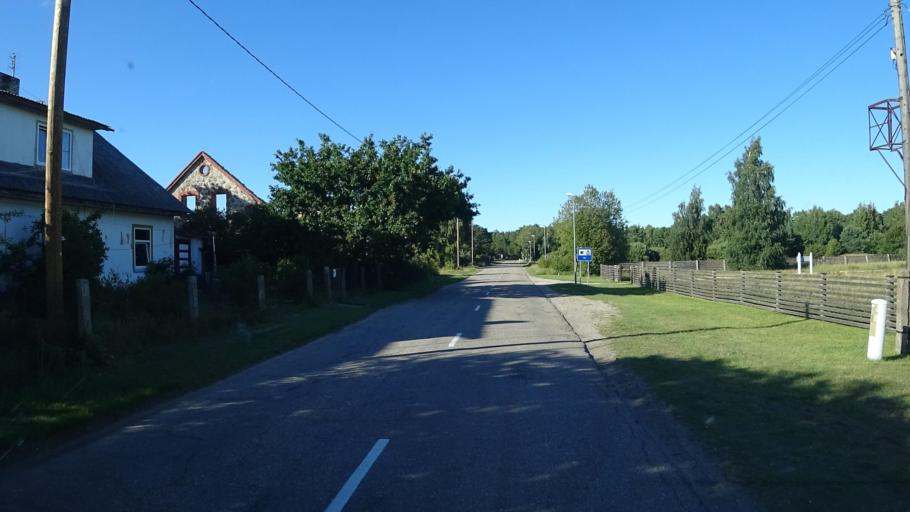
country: LV
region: Rojas
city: Roja
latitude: 57.7487
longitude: 22.5933
